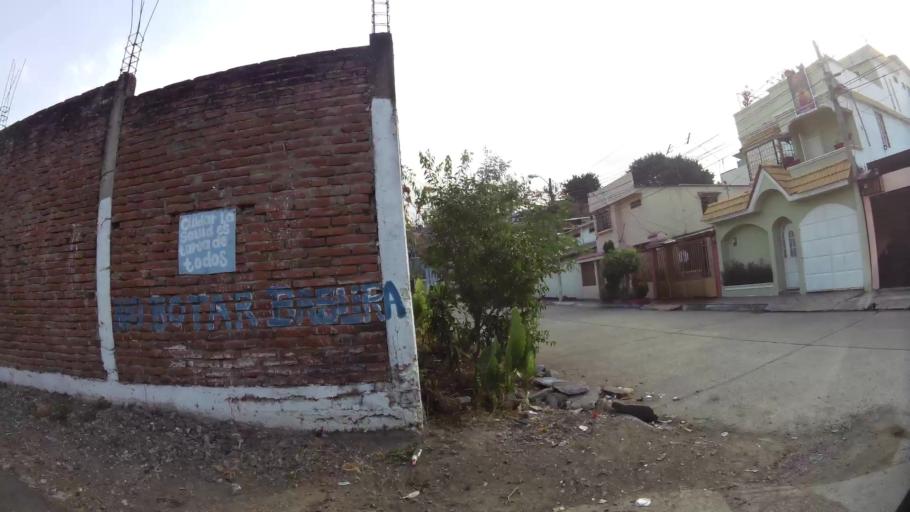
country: EC
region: Guayas
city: Guayaquil
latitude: -2.1531
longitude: -79.9124
